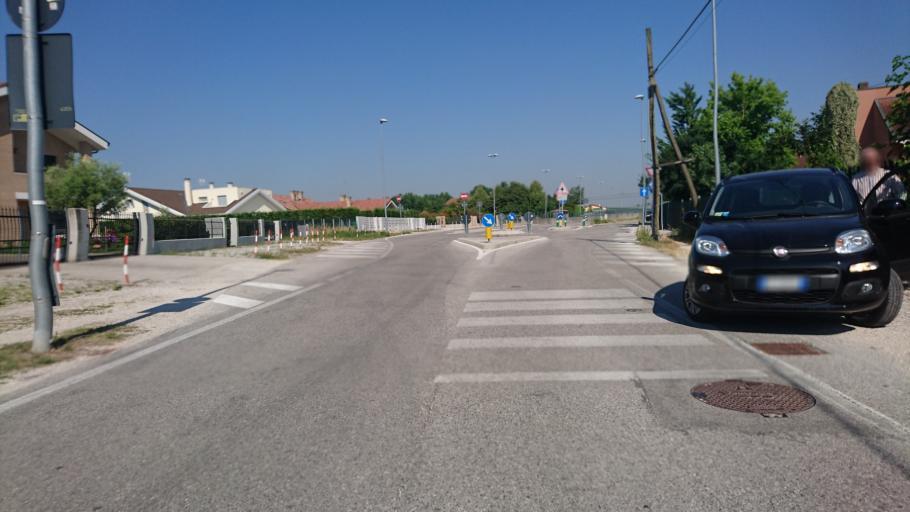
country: IT
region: Veneto
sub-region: Provincia di Padova
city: Mandriola-Sant'Agostino
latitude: 45.3690
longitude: 11.8242
